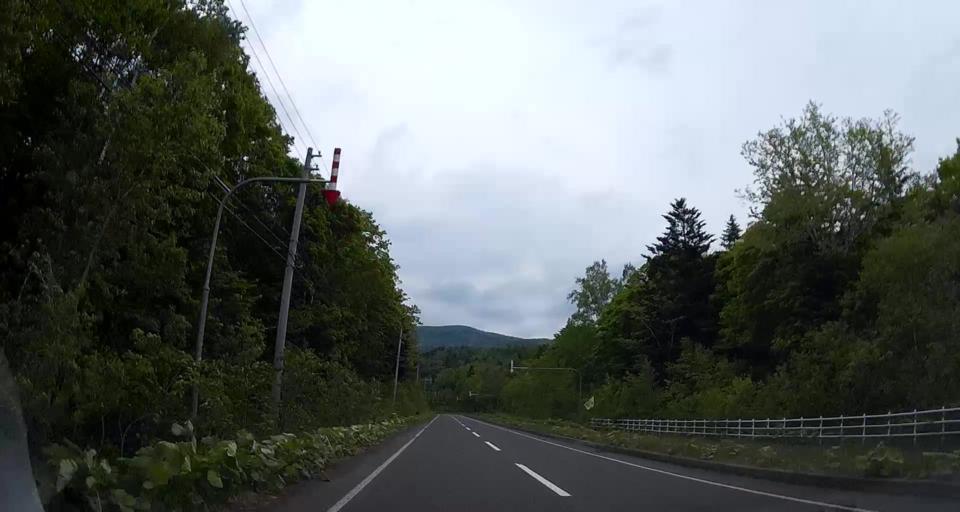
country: JP
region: Hokkaido
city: Shiraoi
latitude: 42.6758
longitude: 141.0966
